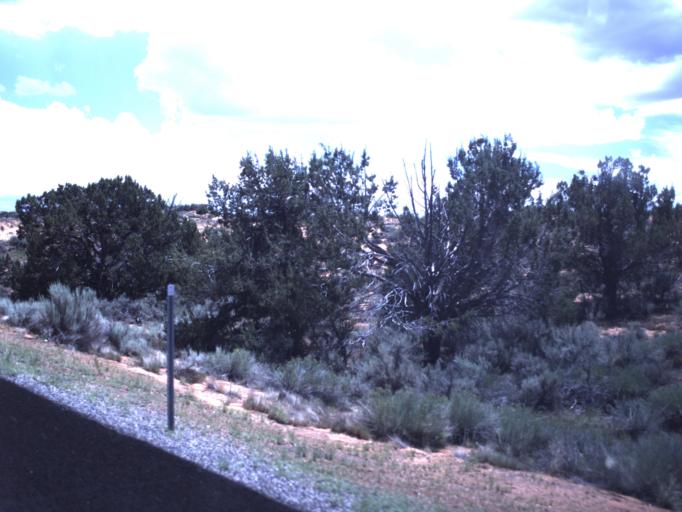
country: US
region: Utah
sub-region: Kane County
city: Kanab
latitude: 37.1691
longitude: -112.6091
